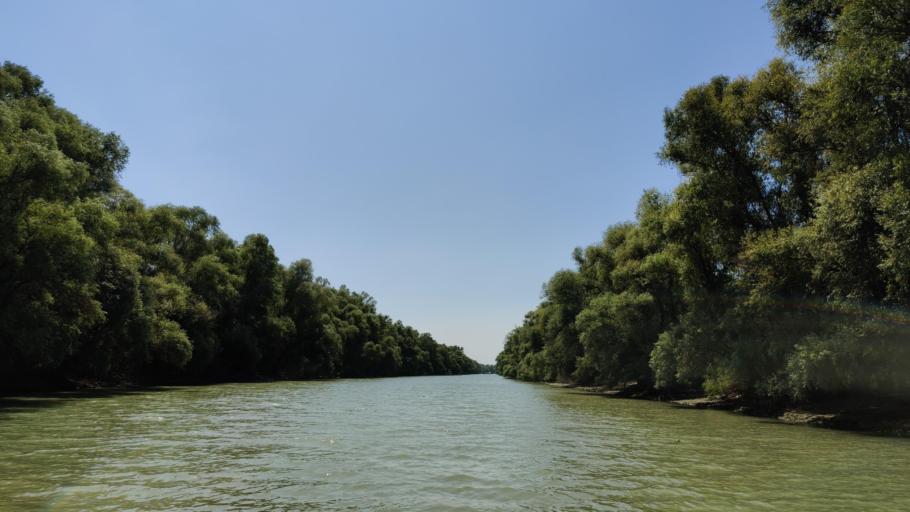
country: RO
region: Tulcea
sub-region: Comuna Pardina
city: Pardina
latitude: 45.2519
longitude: 28.9253
